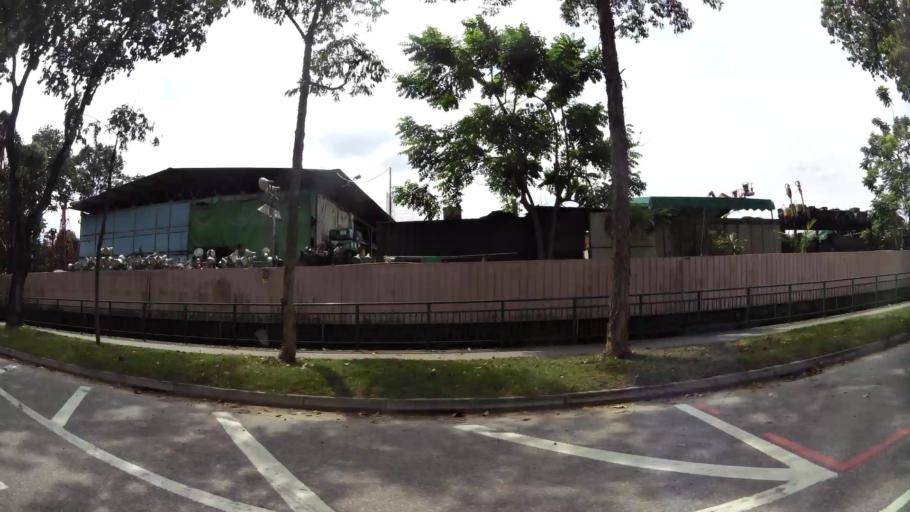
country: MY
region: Johor
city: Johor Bahru
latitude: 1.4242
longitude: 103.7499
